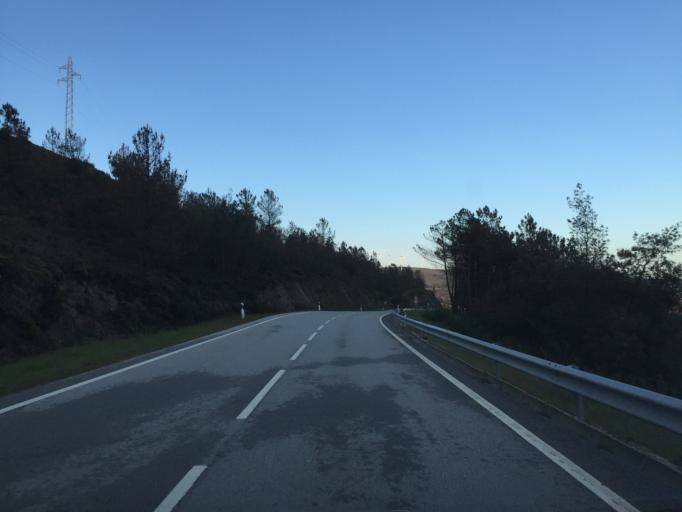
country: PT
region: Coimbra
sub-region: Gois
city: Gois
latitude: 40.1028
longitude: -8.0442
